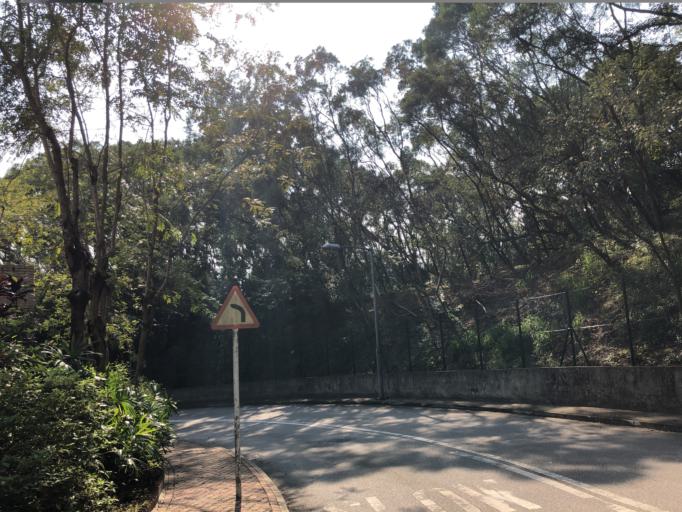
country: HK
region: Tai Po
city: Tai Po
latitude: 22.4675
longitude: 114.1931
